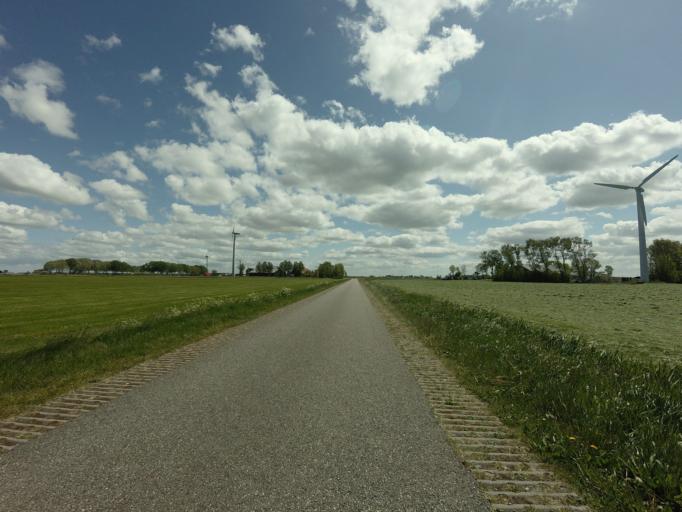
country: NL
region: Friesland
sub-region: Sudwest Fryslan
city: Makkum
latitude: 53.0924
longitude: 5.4095
